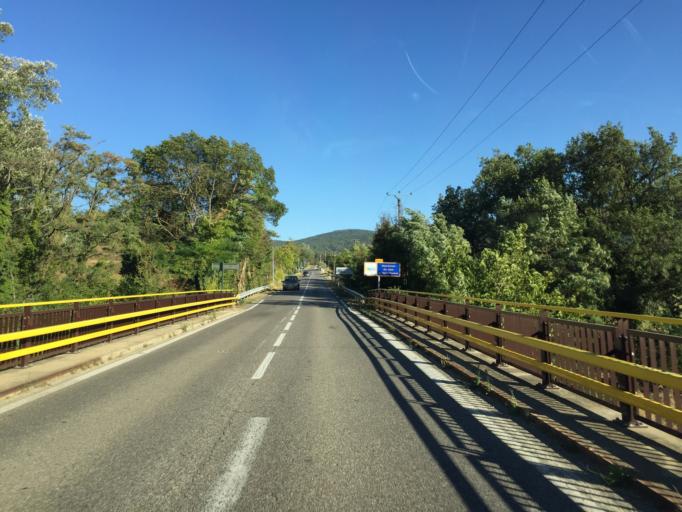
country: FR
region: Provence-Alpes-Cote d'Azur
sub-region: Departement des Alpes-de-Haute-Provence
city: Cereste
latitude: 43.8574
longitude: 5.5614
